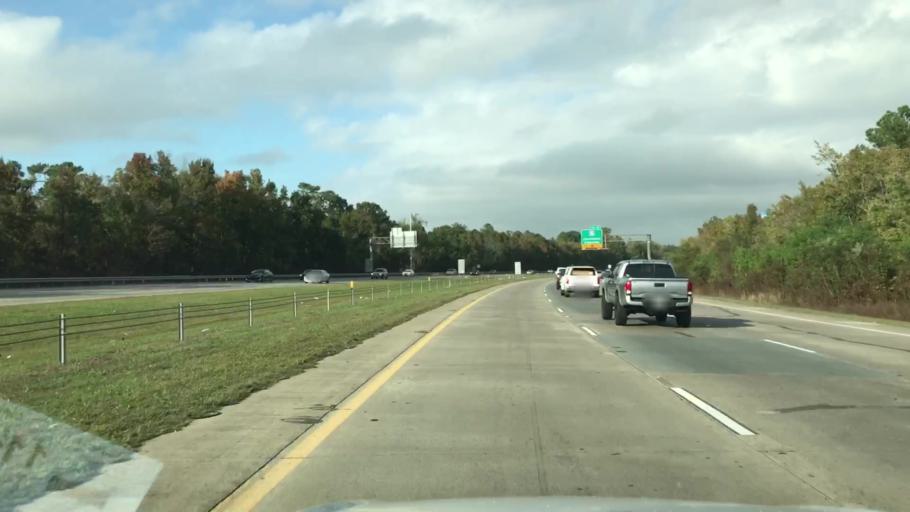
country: US
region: South Carolina
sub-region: Berkeley County
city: Hanahan
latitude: 32.8743
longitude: -80.0266
